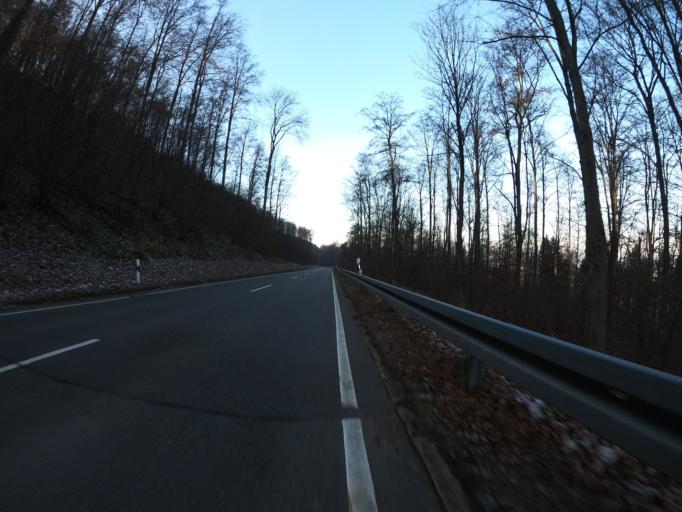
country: DE
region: Baden-Wuerttemberg
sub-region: Regierungsbezirk Stuttgart
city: Eschenbach
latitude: 48.6287
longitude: 9.6718
